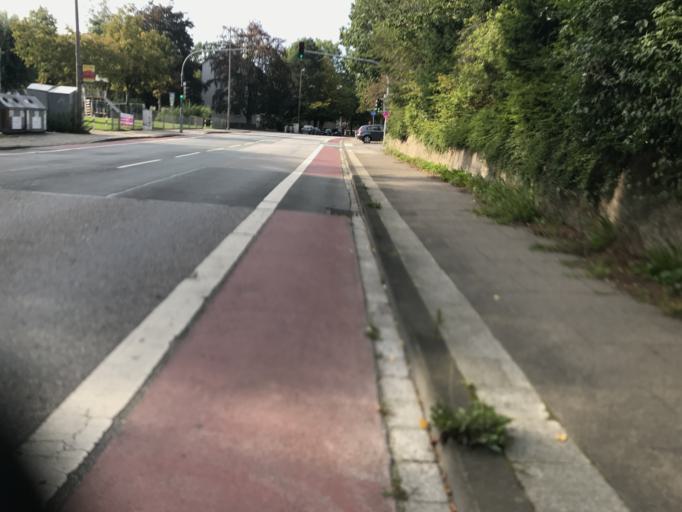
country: DE
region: North Rhine-Westphalia
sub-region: Regierungsbezirk Detmold
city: Herford
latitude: 52.1110
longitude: 8.6544
